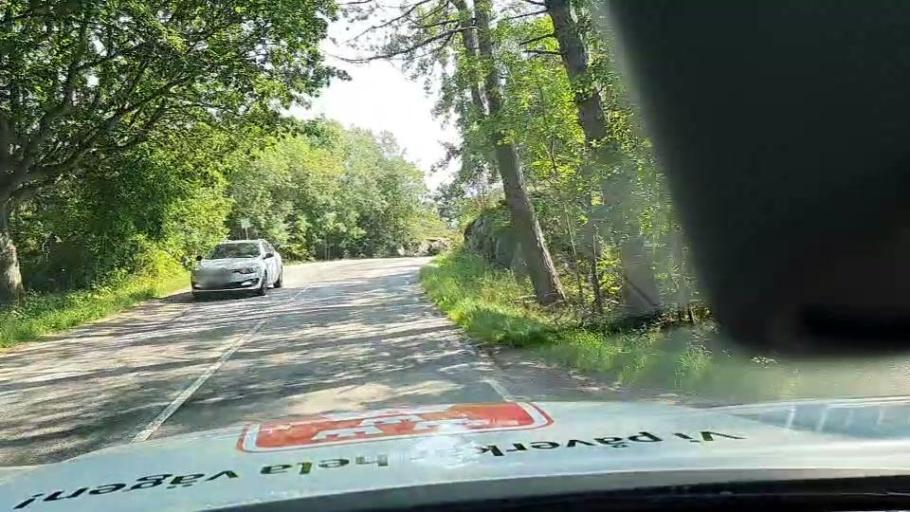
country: SE
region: Vaestra Goetaland
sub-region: Tjorns Kommun
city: Skaerhamn
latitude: 58.0911
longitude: 11.4857
